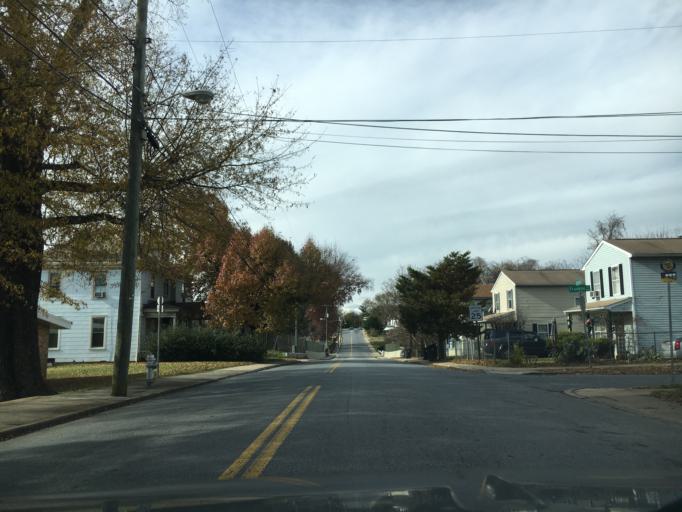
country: US
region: Virginia
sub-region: City of Lynchburg
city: Lynchburg
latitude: 37.4027
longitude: -79.1397
